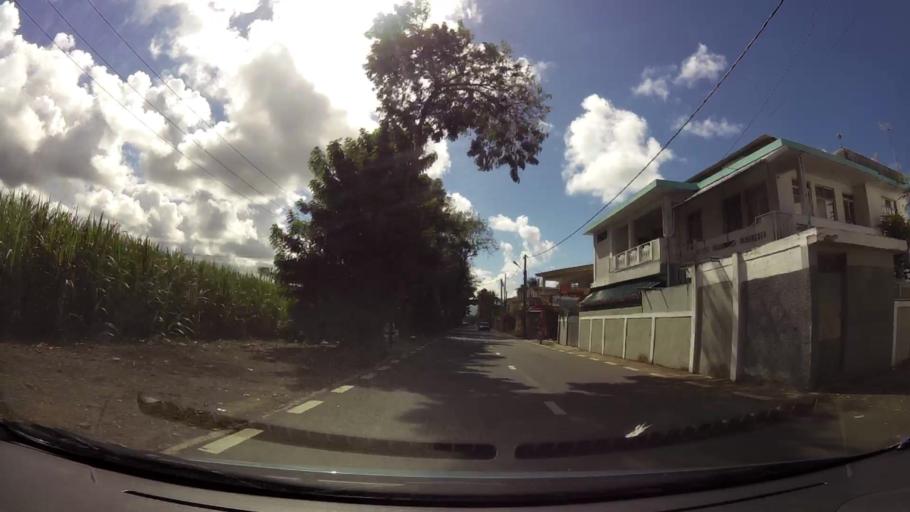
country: MU
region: Grand Port
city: Plaine Magnien
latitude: -20.4282
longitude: 57.6674
